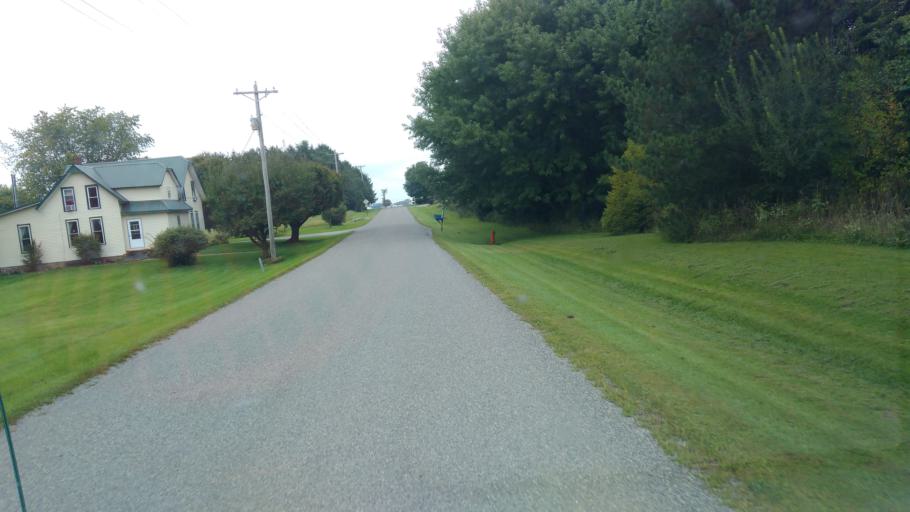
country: US
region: Ohio
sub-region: Hardin County
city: Kenton
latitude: 40.5767
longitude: -83.6801
